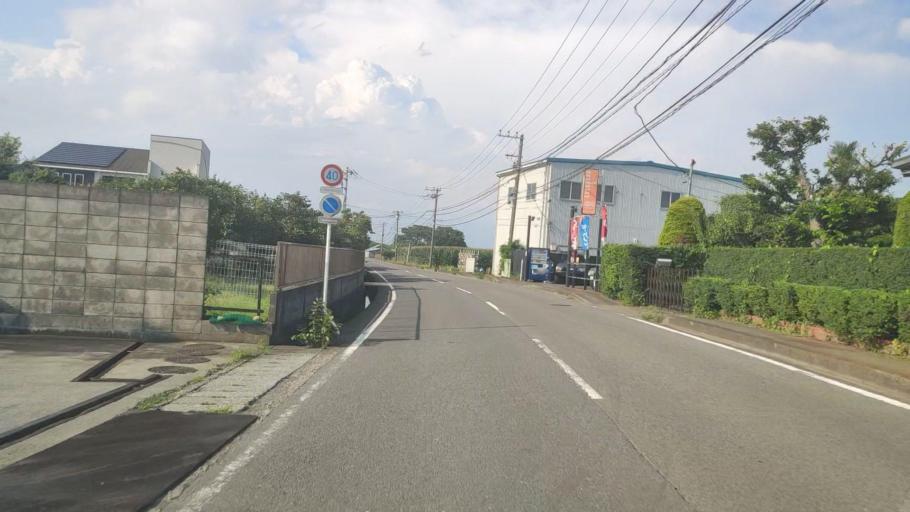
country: JP
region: Kanagawa
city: Isehara
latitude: 35.3802
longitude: 139.3375
